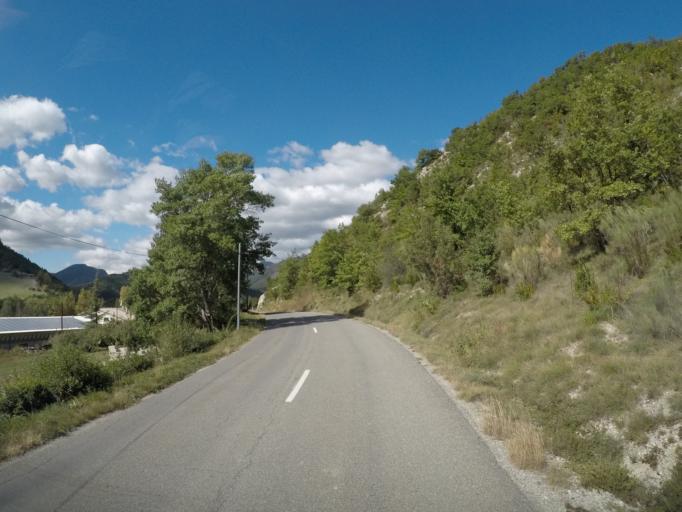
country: FR
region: Provence-Alpes-Cote d'Azur
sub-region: Departement des Hautes-Alpes
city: Laragne-Monteglin
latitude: 44.1676
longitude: 5.7634
